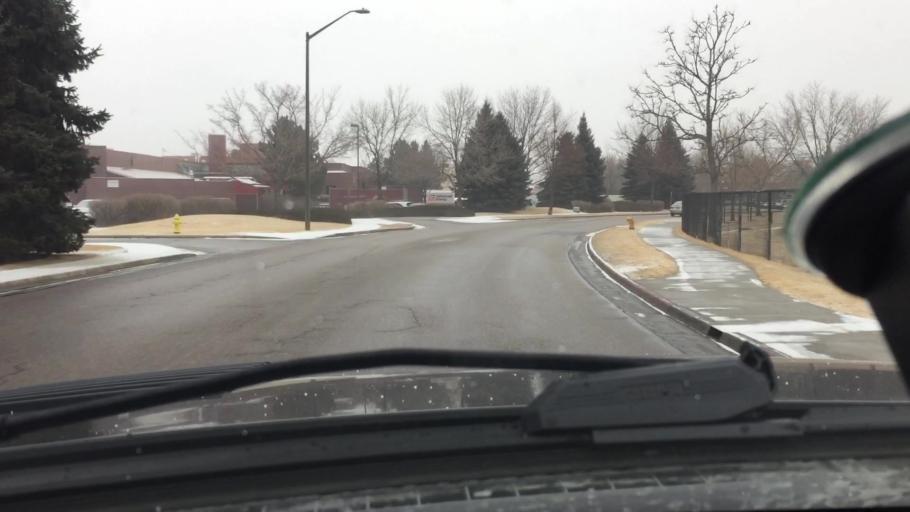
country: US
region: Colorado
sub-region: Larimer County
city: Fort Collins
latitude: 40.5649
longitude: -105.0326
